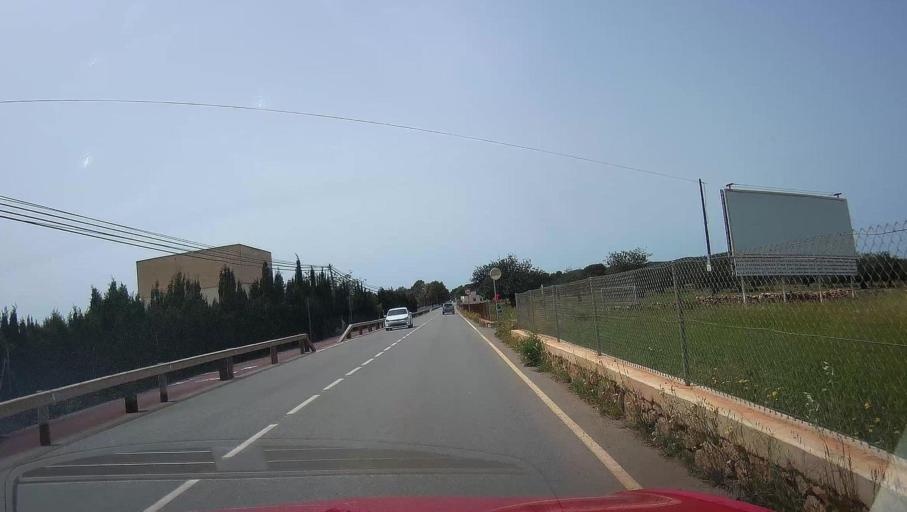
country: ES
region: Balearic Islands
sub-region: Illes Balears
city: Santa Eularia des Riu
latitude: 39.0035
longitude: 1.5689
